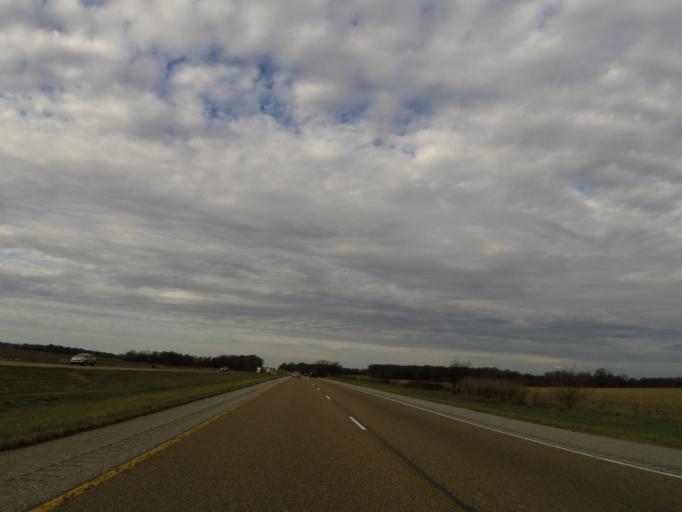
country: US
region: Illinois
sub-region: Clinton County
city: Wamac
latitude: 38.3889
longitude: -89.1973
